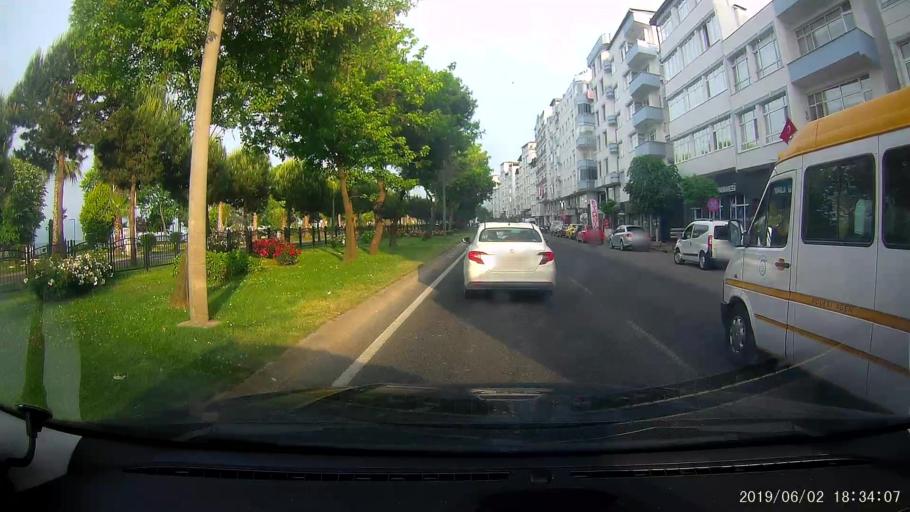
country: TR
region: Ordu
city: Fatsa
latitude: 41.0311
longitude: 37.5011
